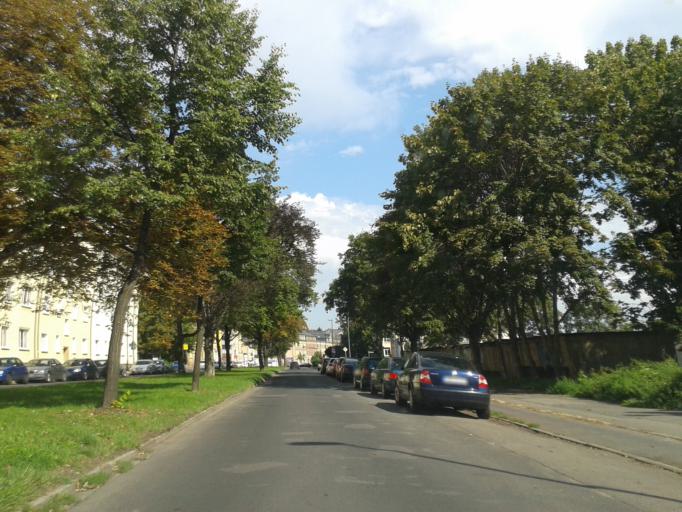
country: DE
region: Saxony
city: Albertstadt
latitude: 51.0413
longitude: 13.7887
